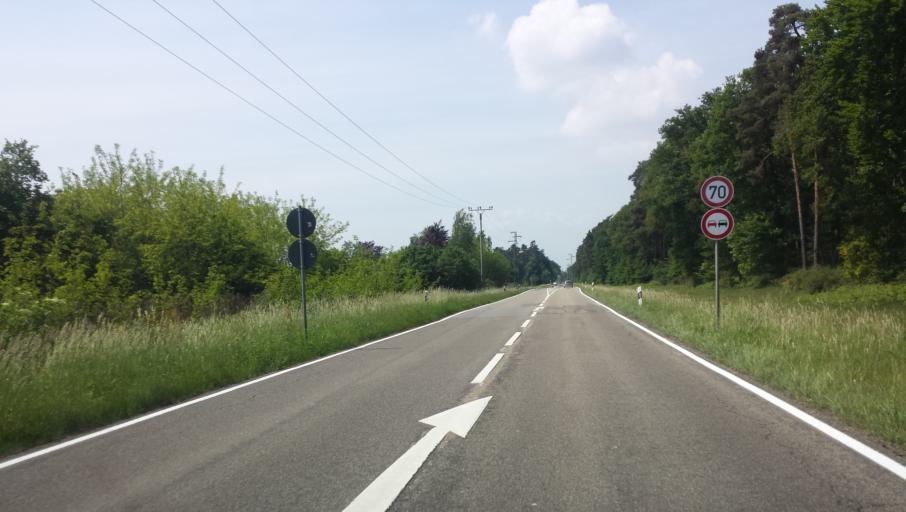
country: DE
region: Rheinland-Pfalz
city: Berg
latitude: 48.9915
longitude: 8.2065
